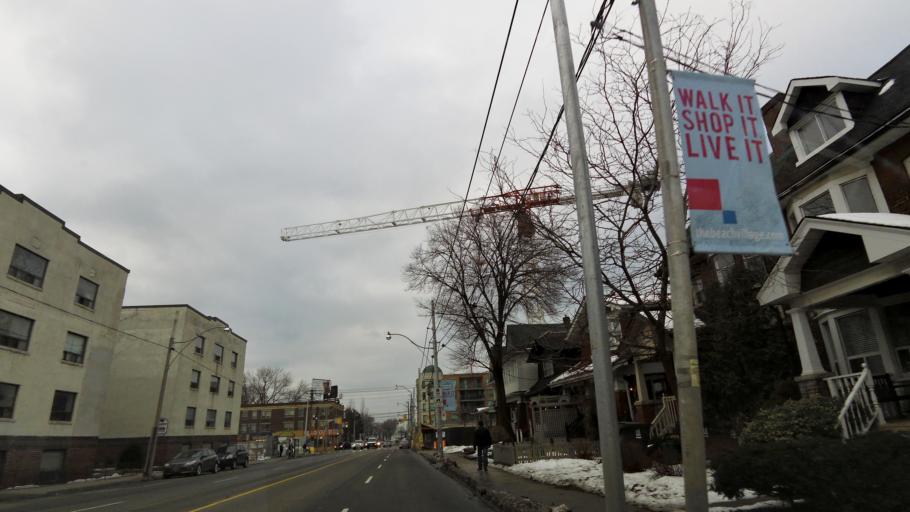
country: CA
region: Ontario
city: Scarborough
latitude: 43.6697
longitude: -79.3062
